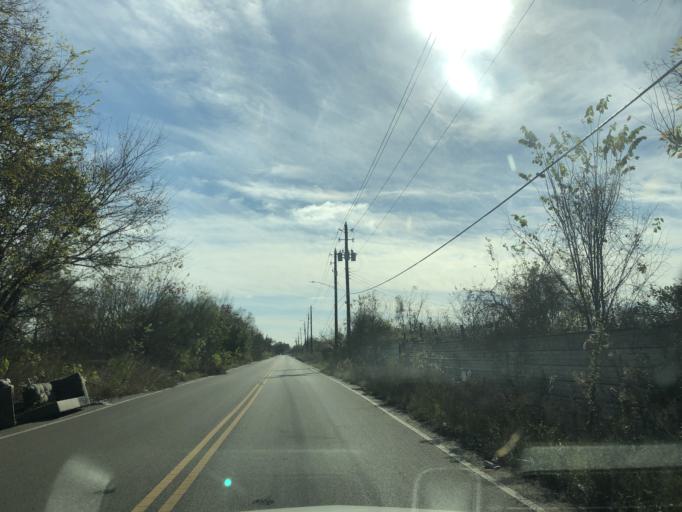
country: US
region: Texas
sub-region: Harris County
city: South Houston
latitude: 29.6600
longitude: -95.2527
